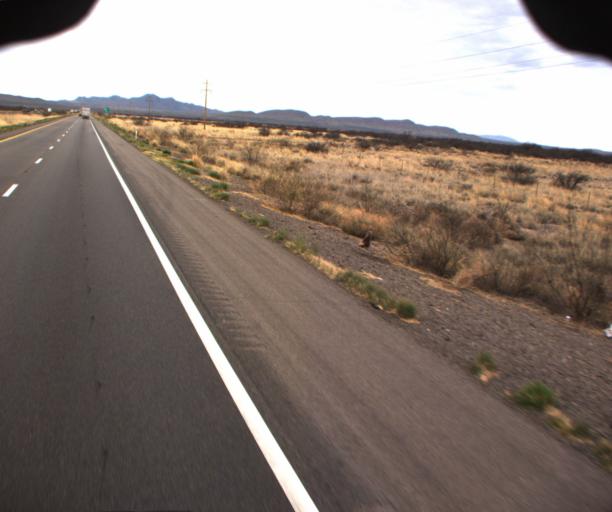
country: US
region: Arizona
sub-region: Cochise County
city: Willcox
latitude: 32.1993
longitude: -109.9114
